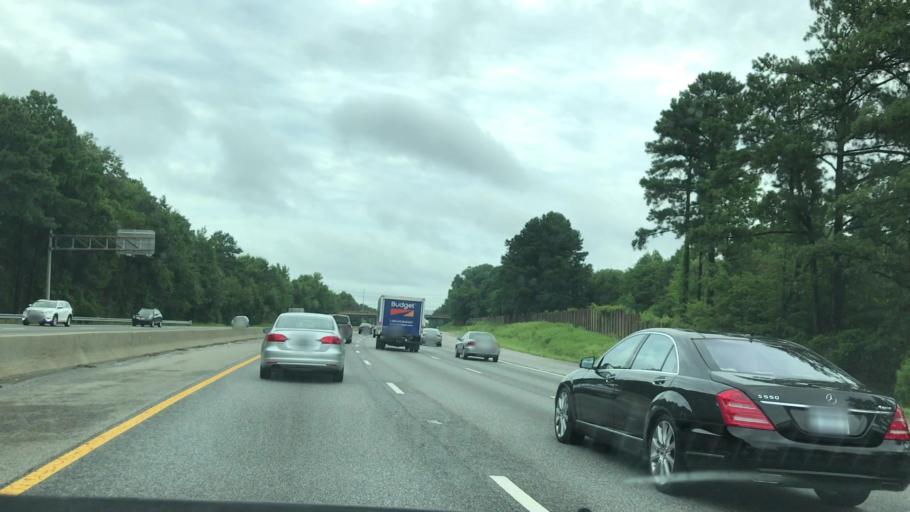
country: US
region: Virginia
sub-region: City of Colonial Heights
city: Colonial Heights
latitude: 37.2619
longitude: -77.3987
